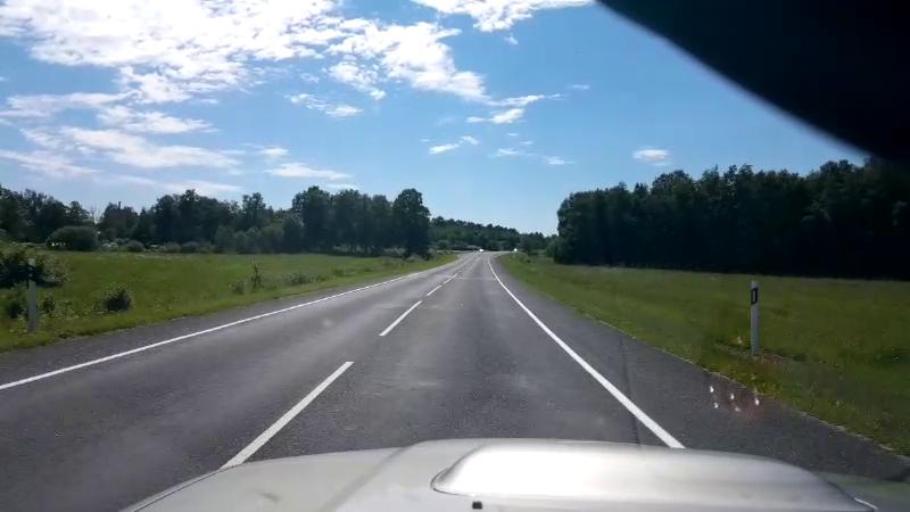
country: EE
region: Jaervamaa
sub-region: Jaerva-Jaani vald
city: Jarva-Jaani
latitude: 59.0513
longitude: 25.8825
